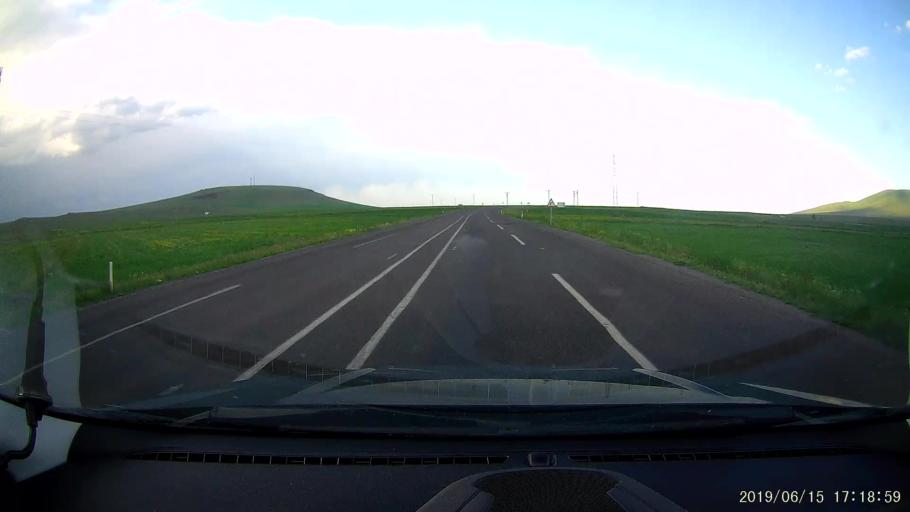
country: TR
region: Kars
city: Kars
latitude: 40.6149
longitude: 43.2695
